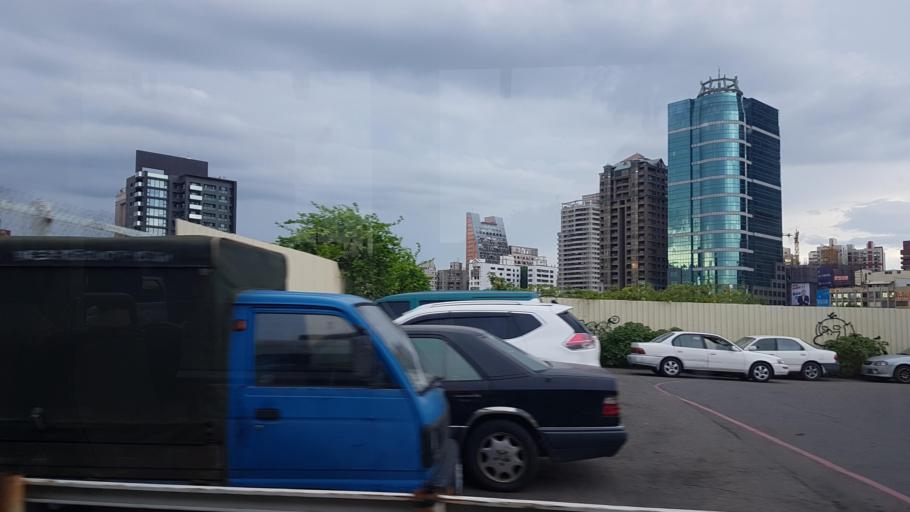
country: TW
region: Kaohsiung
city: Kaohsiung
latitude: 22.6101
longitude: 120.2967
